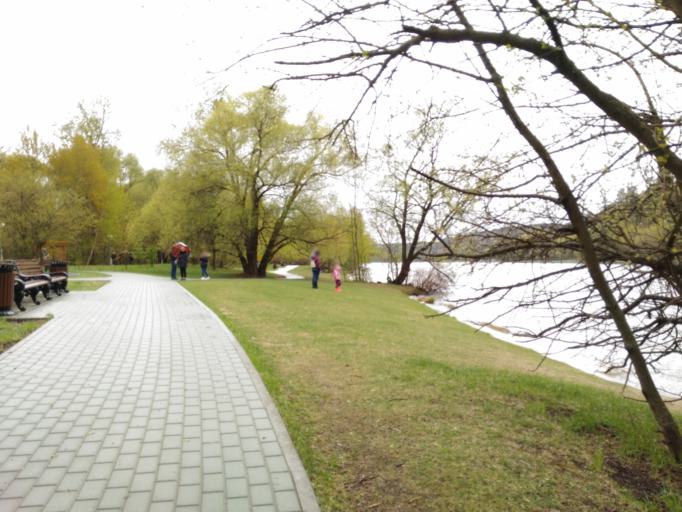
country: RU
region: Moscow
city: Strogino
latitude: 55.7896
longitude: 37.4103
